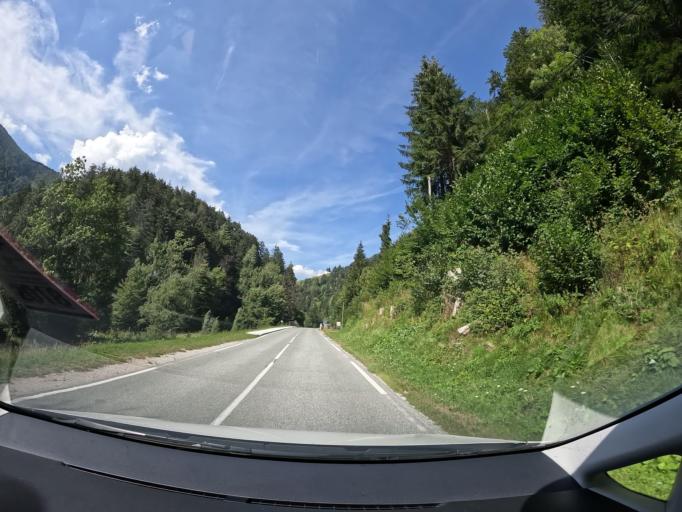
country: SI
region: Preddvor
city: Preddvor
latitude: 46.3695
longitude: 14.4115
